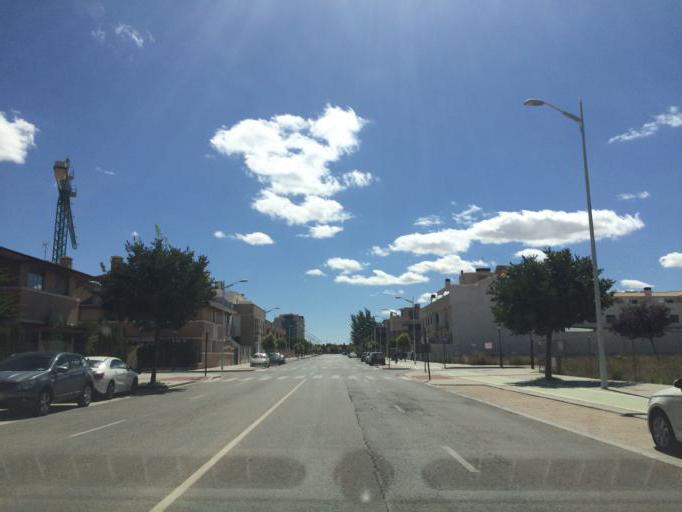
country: ES
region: Castille-La Mancha
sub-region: Provincia de Albacete
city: Albacete
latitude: 38.9814
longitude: -1.8418
